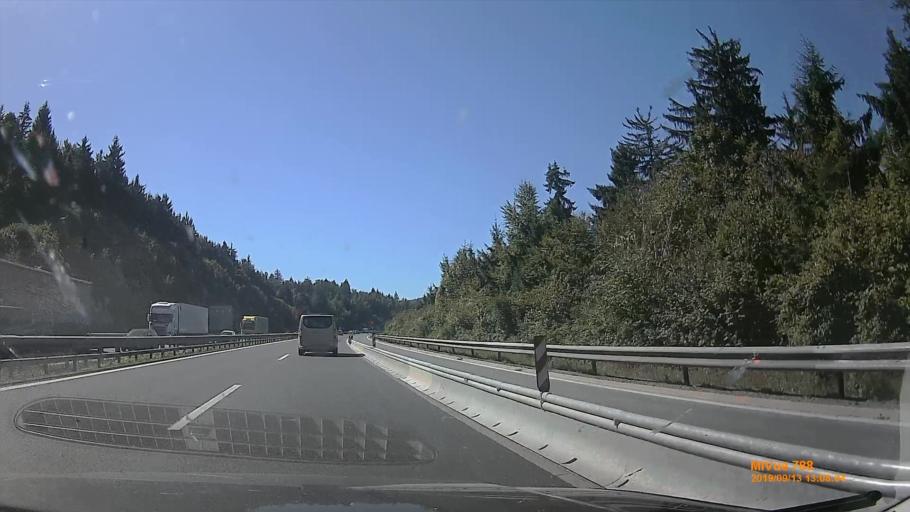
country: SI
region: Vrhnika
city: Verd
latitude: 45.9486
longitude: 14.2977
